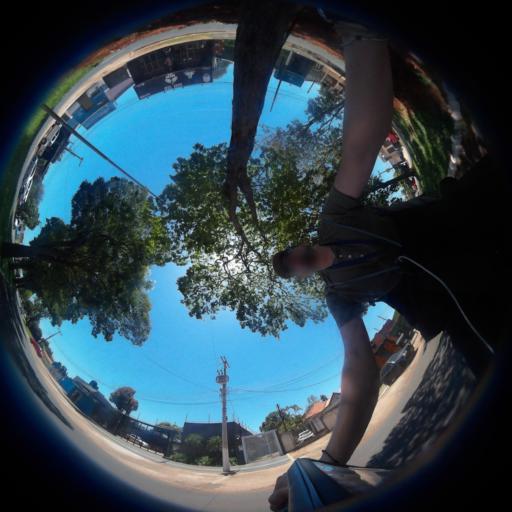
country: BR
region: Mato Grosso do Sul
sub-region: Ponta Pora
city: Ponta Pora
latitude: -22.5285
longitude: -55.7348
